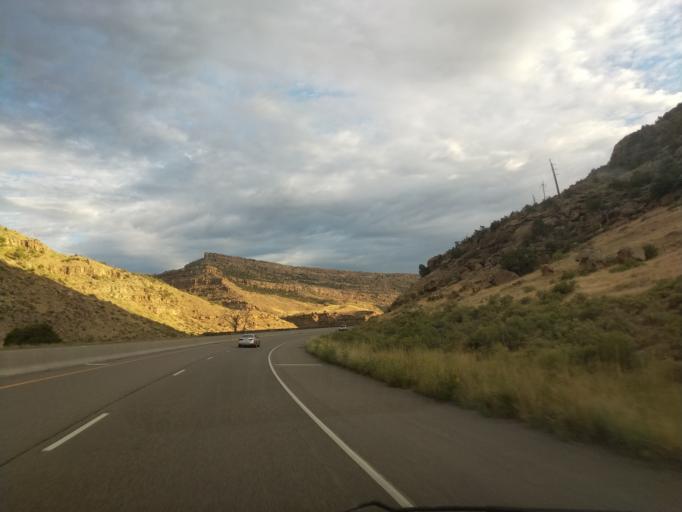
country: US
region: Colorado
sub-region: Mesa County
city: Palisade
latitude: 39.2312
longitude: -108.2706
